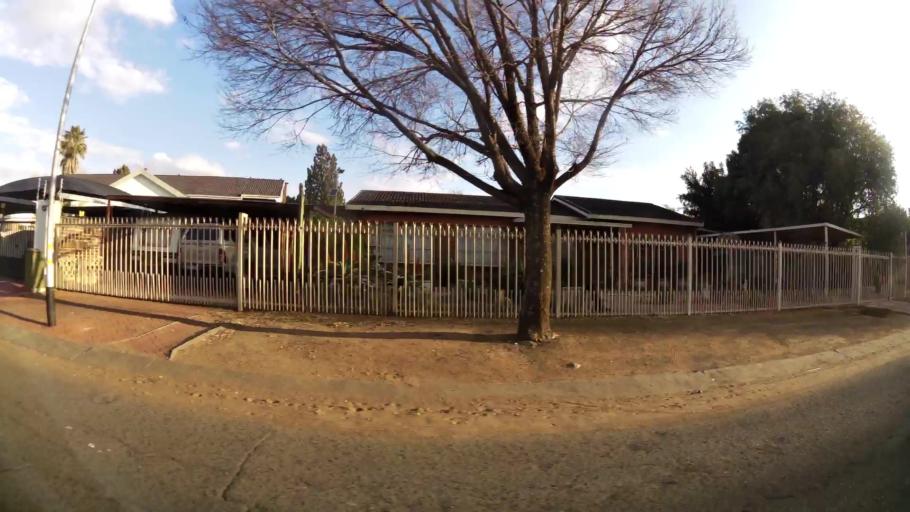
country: ZA
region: Orange Free State
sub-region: Mangaung Metropolitan Municipality
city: Bloemfontein
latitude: -29.1544
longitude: 26.1863
